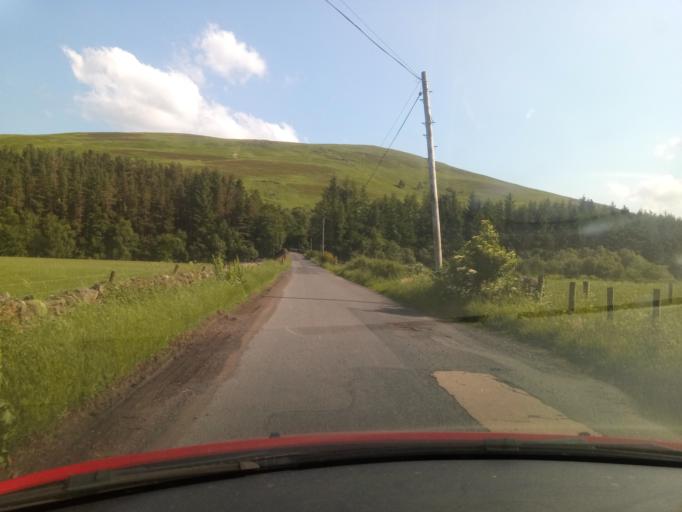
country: GB
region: Scotland
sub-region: The Scottish Borders
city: Innerleithen
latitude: 55.5128
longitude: -3.0970
